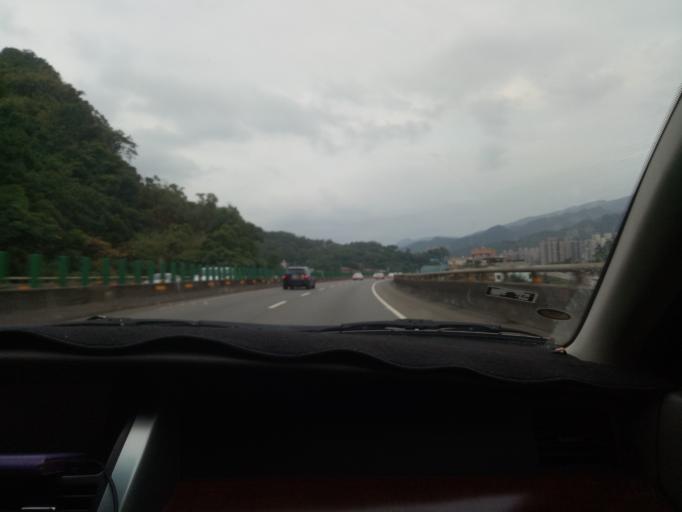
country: TW
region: Taiwan
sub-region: Keelung
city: Keelung
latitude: 25.1031
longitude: 121.7431
